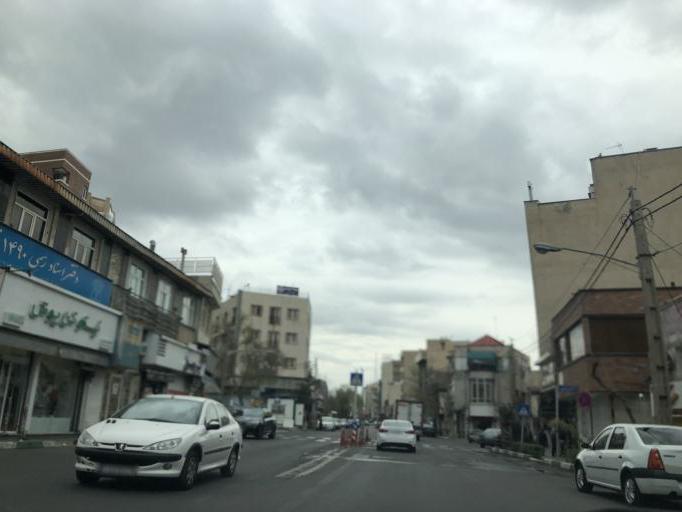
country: IR
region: Tehran
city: Tajrish
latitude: 35.7795
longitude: 51.4462
